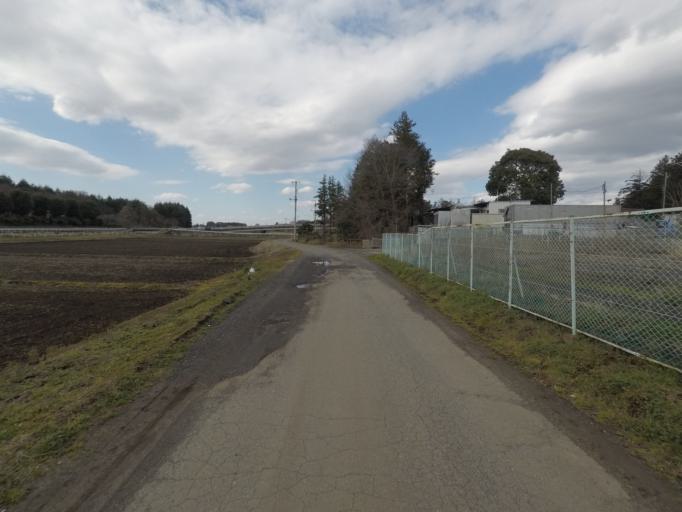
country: JP
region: Ibaraki
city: Ushiku
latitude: 36.0124
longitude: 140.1151
